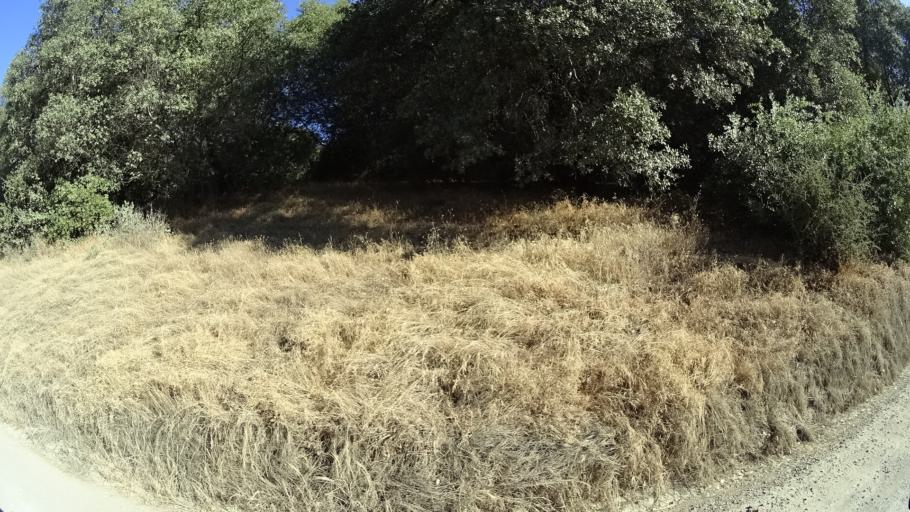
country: US
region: California
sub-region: Calaveras County
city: Angels Camp
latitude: 38.0627
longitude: -120.4995
